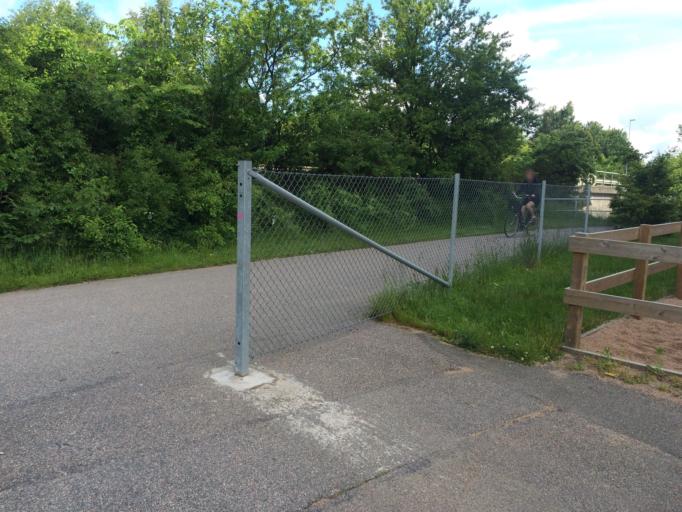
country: SE
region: Halland
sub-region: Halmstads Kommun
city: Halmstad
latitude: 56.6726
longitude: 12.8438
